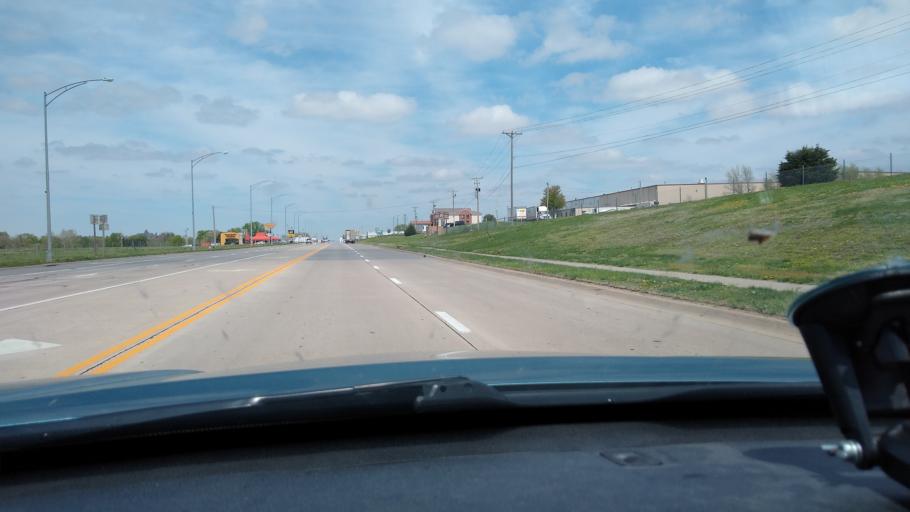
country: US
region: Kansas
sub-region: Cloud County
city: Concordia
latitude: 39.5524
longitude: -97.6574
